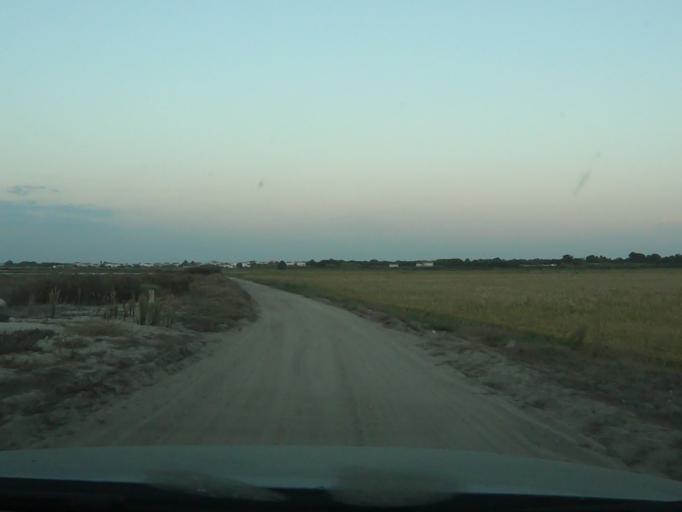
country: PT
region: Setubal
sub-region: Setubal
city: Setubal
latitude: 38.4065
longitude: -8.7636
